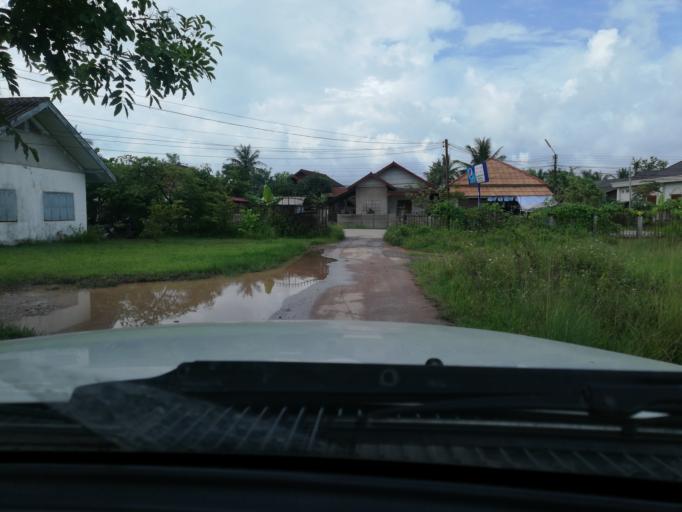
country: LA
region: Loungnamtha
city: Louang Namtha
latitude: 20.9517
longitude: 101.4006
